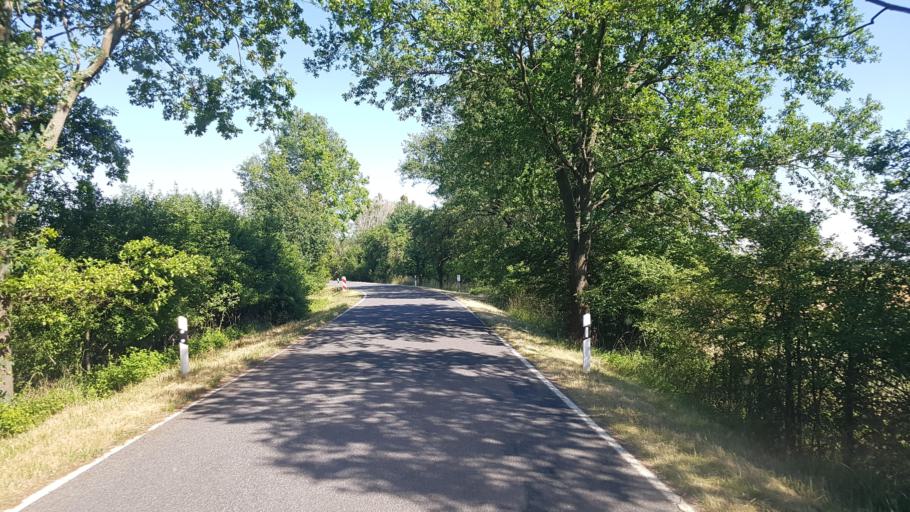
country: DE
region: Saxony-Anhalt
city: Elster
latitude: 51.7677
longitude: 12.8473
